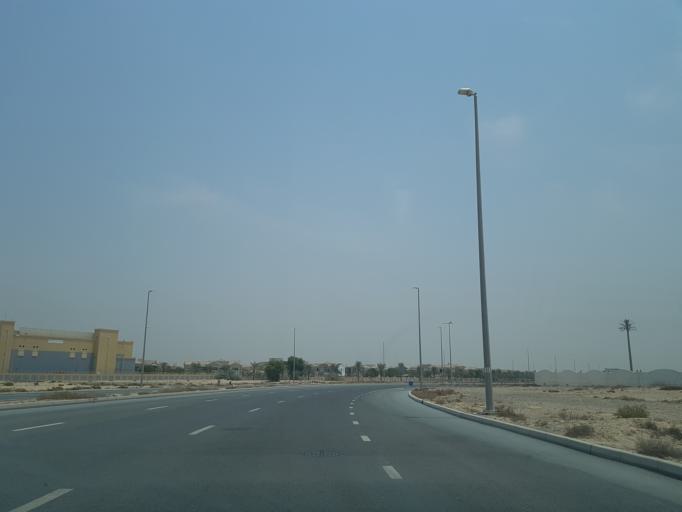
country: AE
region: Dubai
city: Dubai
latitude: 25.0373
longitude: 55.2457
